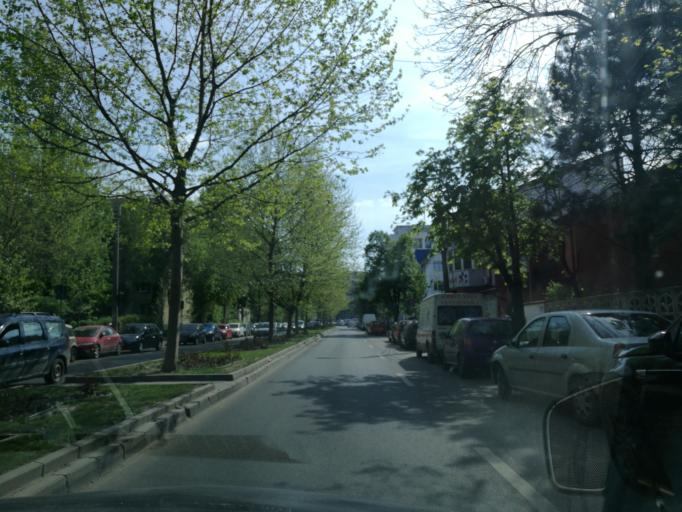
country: RO
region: Ilfov
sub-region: Comuna Chiajna
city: Rosu
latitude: 44.4365
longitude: 26.0220
